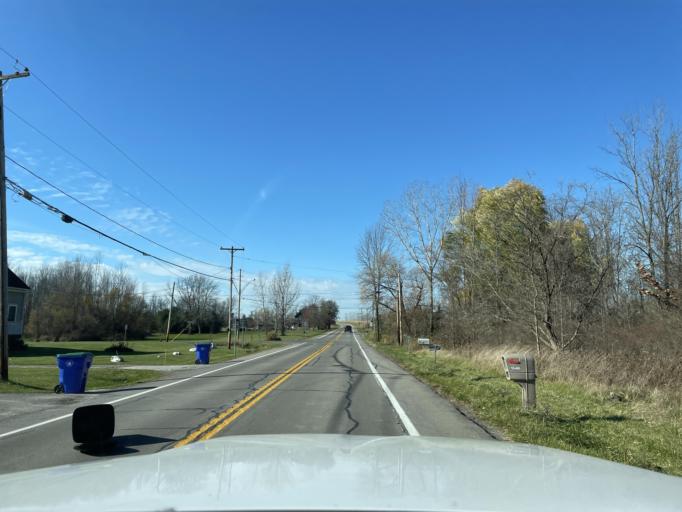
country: US
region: New York
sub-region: Niagara County
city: Middleport
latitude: 43.2160
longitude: -78.4465
